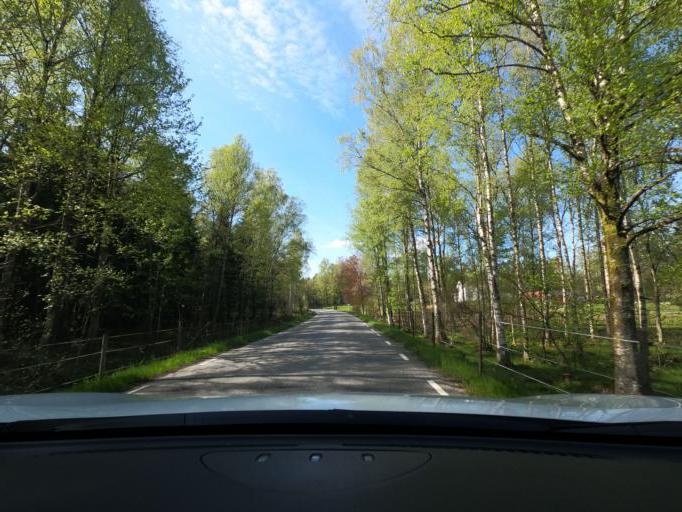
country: SE
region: Vaestra Goetaland
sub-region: Marks Kommun
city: Bua
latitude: 57.4887
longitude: 12.5632
